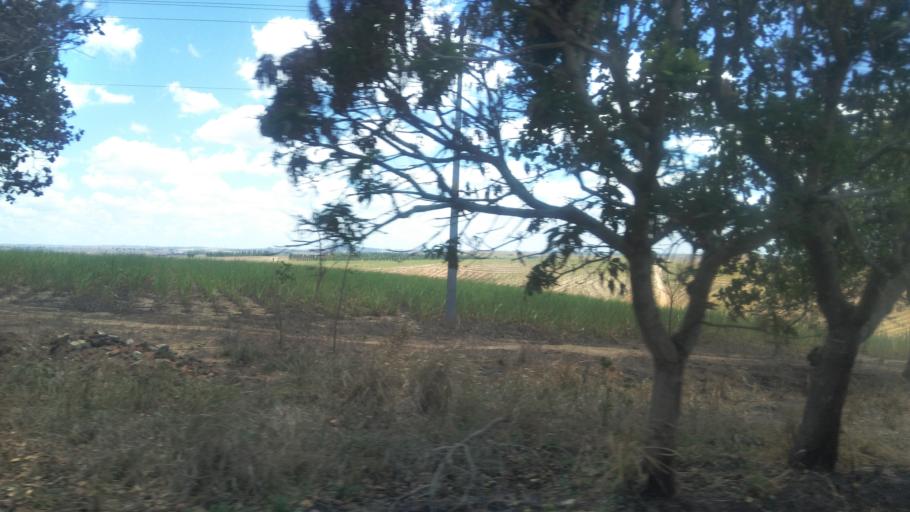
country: BR
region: Pernambuco
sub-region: Nazare Da Mata
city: Nazare da Mata
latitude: -7.7332
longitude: -35.2642
